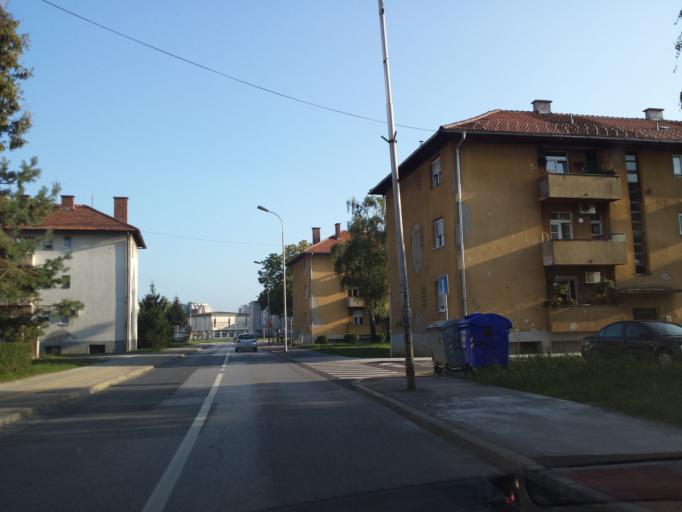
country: HR
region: Karlovacka
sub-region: Grad Karlovac
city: Karlovac
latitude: 45.4906
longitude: 15.5432
